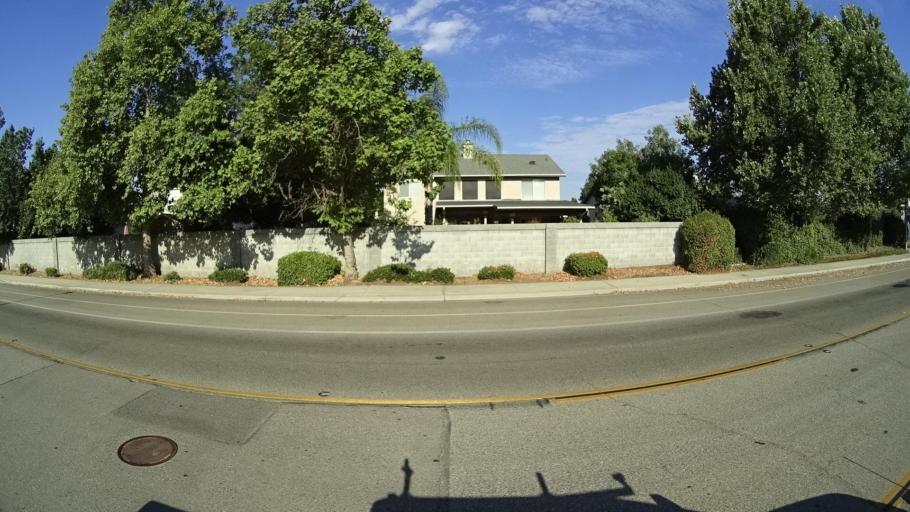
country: US
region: California
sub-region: Fresno County
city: Tarpey Village
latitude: 36.7912
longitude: -119.6550
